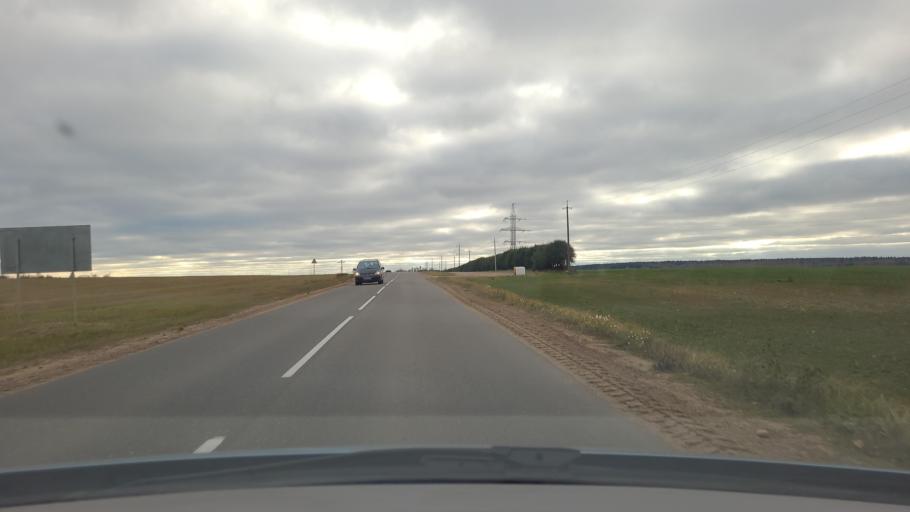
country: BY
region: Minsk
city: Krupki
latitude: 54.3642
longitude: 29.0536
